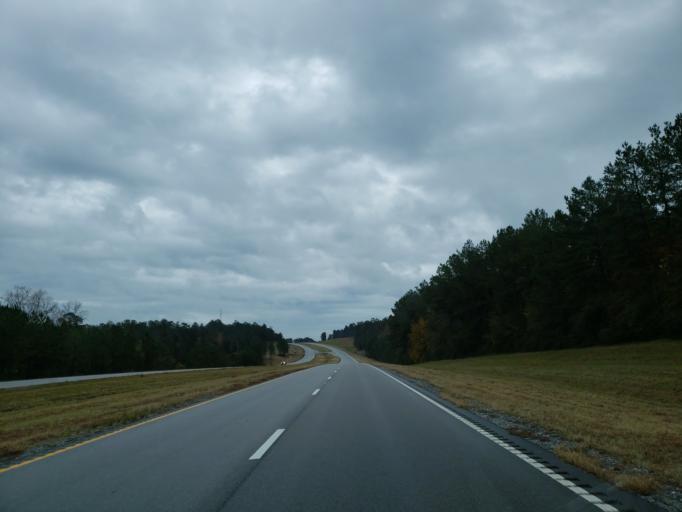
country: US
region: Mississippi
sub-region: Wayne County
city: Waynesboro
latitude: 31.6872
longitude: -88.7045
